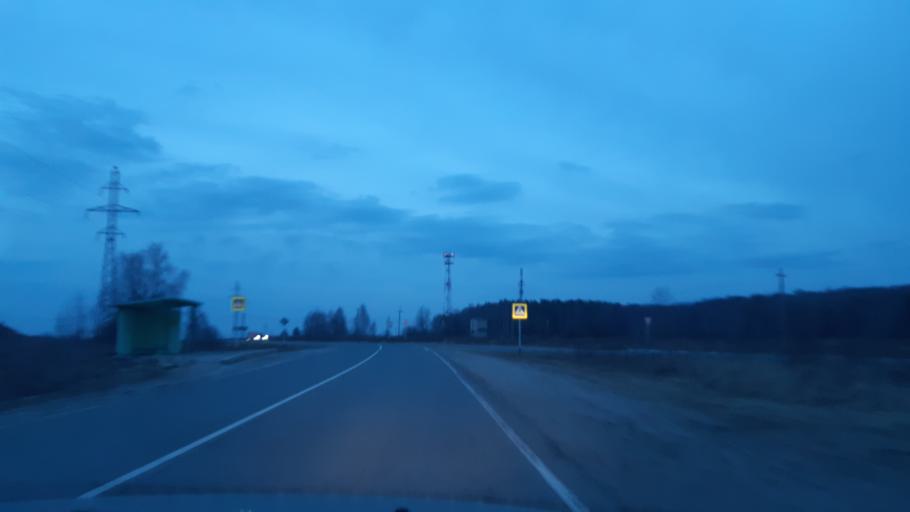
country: RU
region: Vladimir
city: Luknovo
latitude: 56.1976
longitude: 42.0334
